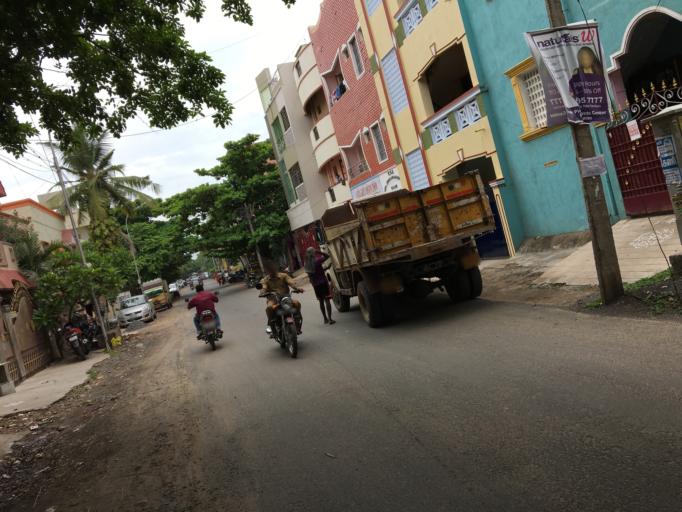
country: IN
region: Tamil Nadu
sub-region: Kancheepuram
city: Alandur
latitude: 12.9899
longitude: 80.2120
